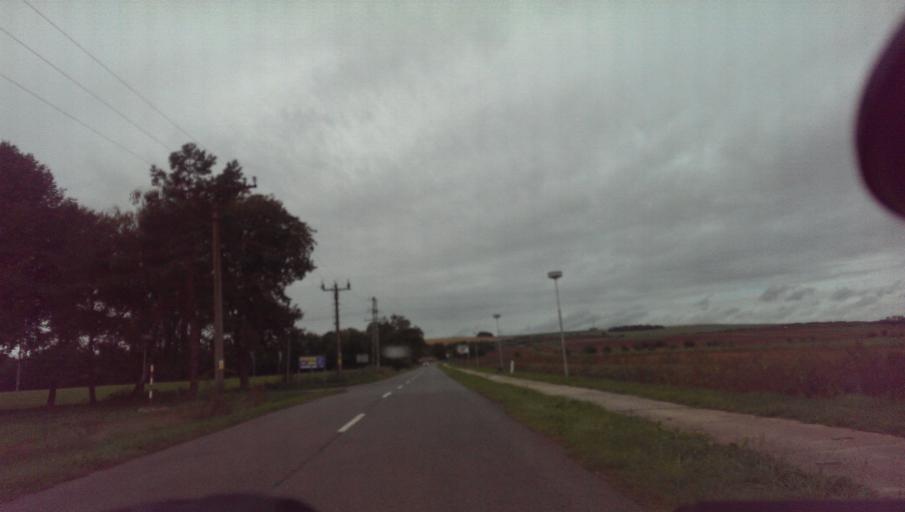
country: CZ
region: South Moravian
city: Moravsky Pisek
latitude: 48.9921
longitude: 17.3268
